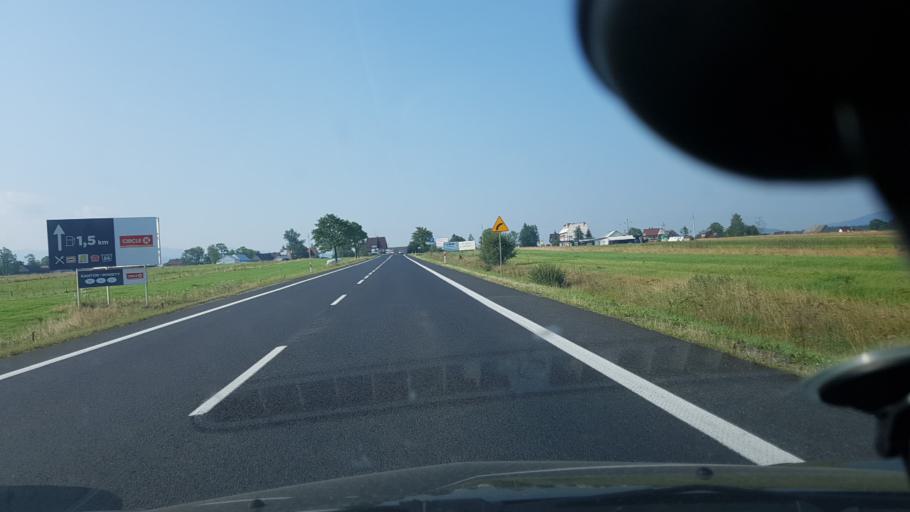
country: PL
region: Lesser Poland Voivodeship
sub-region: Powiat nowotarski
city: Chyzne
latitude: 49.4305
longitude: 19.6768
